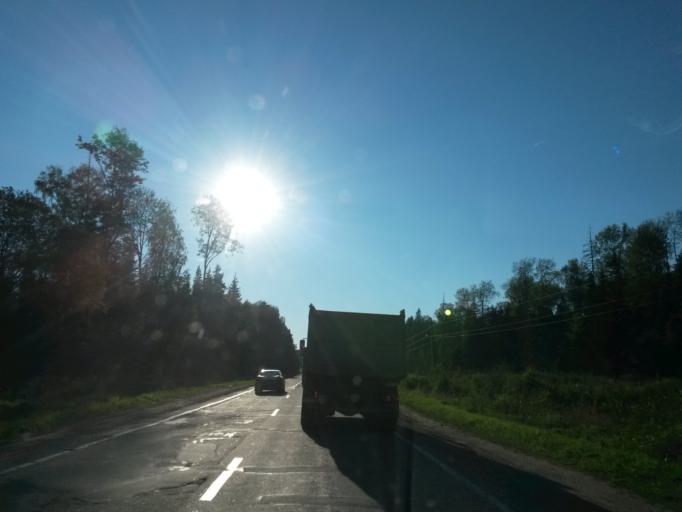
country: RU
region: Jaroslavl
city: Gavrilov-Yam
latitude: 57.2654
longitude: 40.0062
